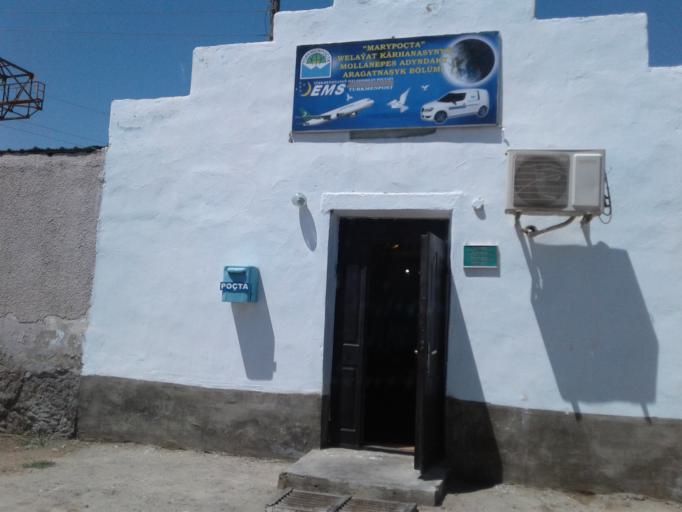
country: TM
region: Mary
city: Mary
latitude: 37.6044
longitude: 61.9240
